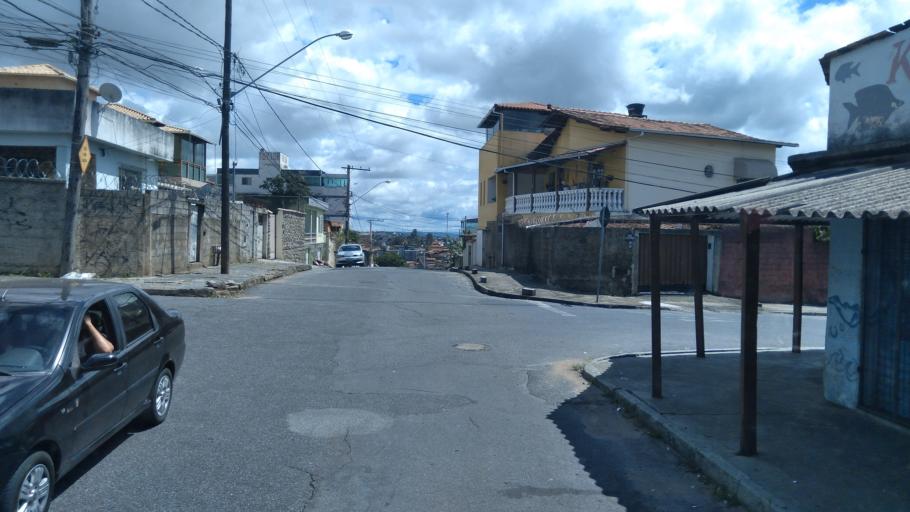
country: BR
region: Minas Gerais
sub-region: Belo Horizonte
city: Belo Horizonte
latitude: -19.8852
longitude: -43.9028
